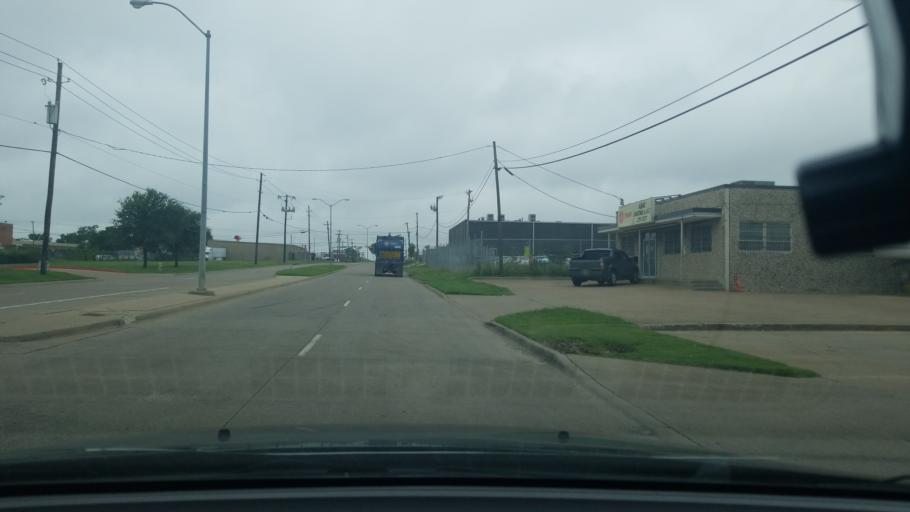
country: US
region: Texas
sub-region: Dallas County
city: Balch Springs
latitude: 32.7781
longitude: -96.6795
